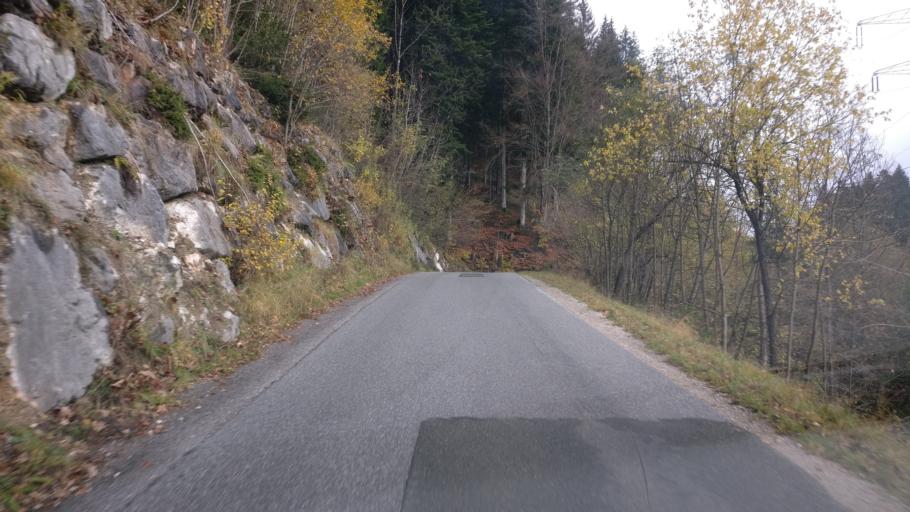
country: AT
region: Salzburg
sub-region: Politischer Bezirk Sankt Johann im Pongau
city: Forstau
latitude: 47.3961
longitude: 13.5100
